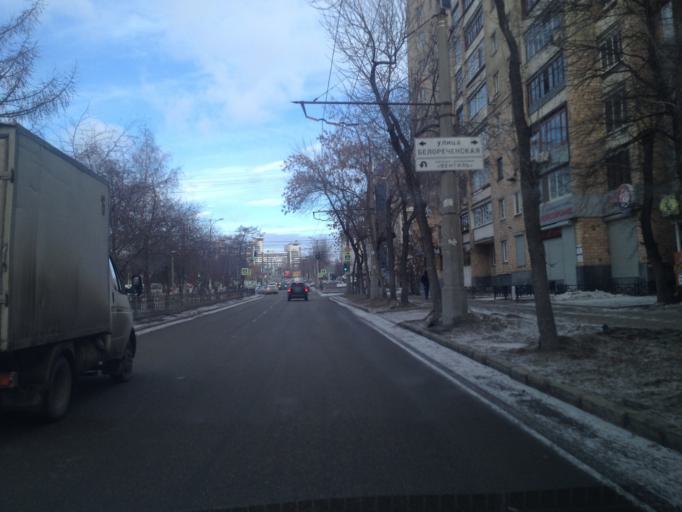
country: RU
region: Sverdlovsk
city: Yekaterinburg
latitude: 56.8223
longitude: 60.5725
